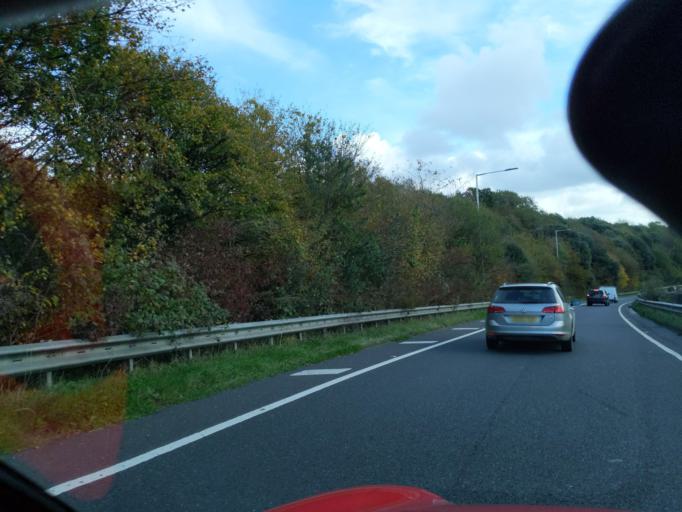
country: GB
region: England
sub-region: Plymouth
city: Plymouth
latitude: 50.4005
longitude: -4.1311
